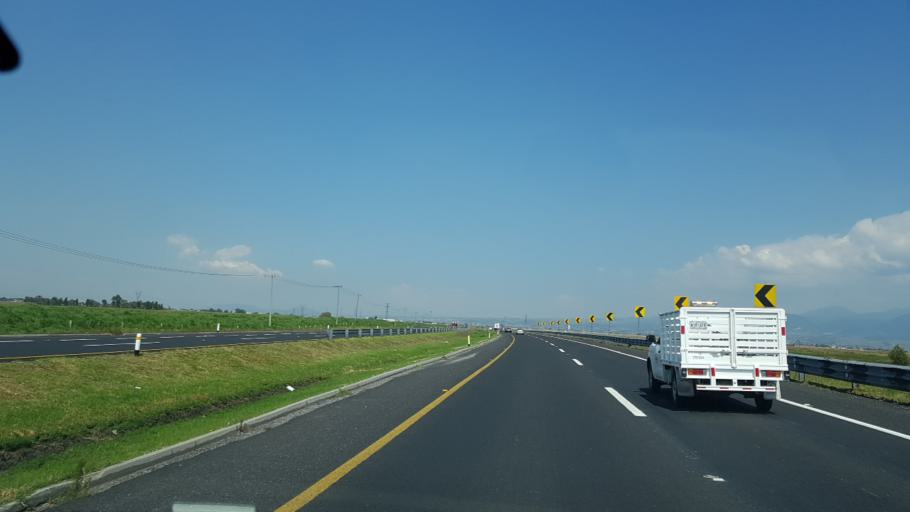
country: MX
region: Mexico
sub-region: Toluca
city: La Constitucion Toltepec
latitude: 19.3487
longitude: -99.5312
